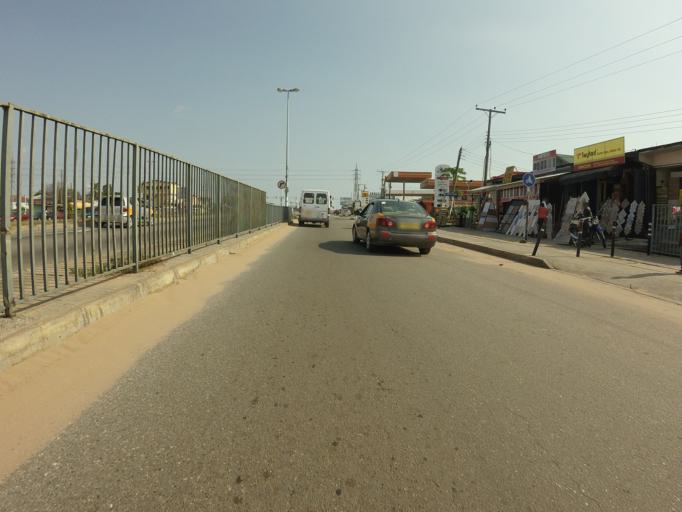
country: GH
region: Greater Accra
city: Gbawe
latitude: 5.6006
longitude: -0.2919
